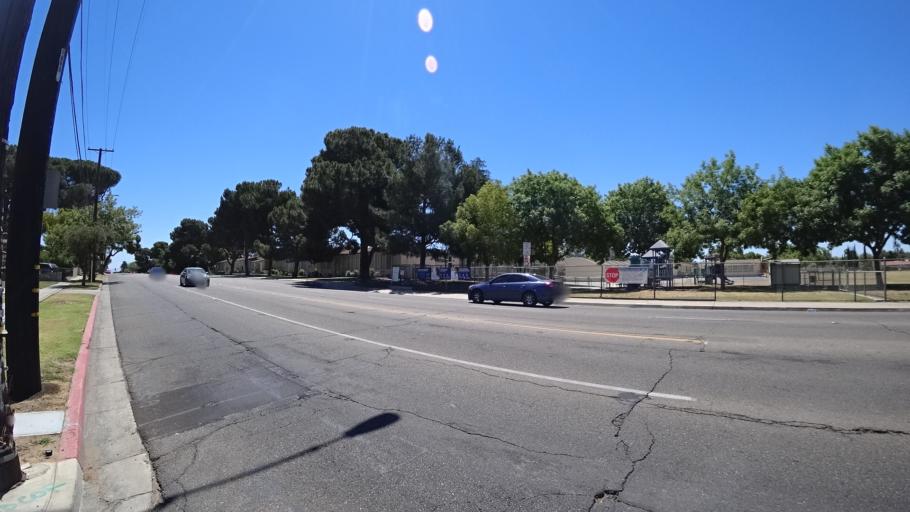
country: US
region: California
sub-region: Fresno County
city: Fresno
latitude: 36.7722
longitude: -119.8119
